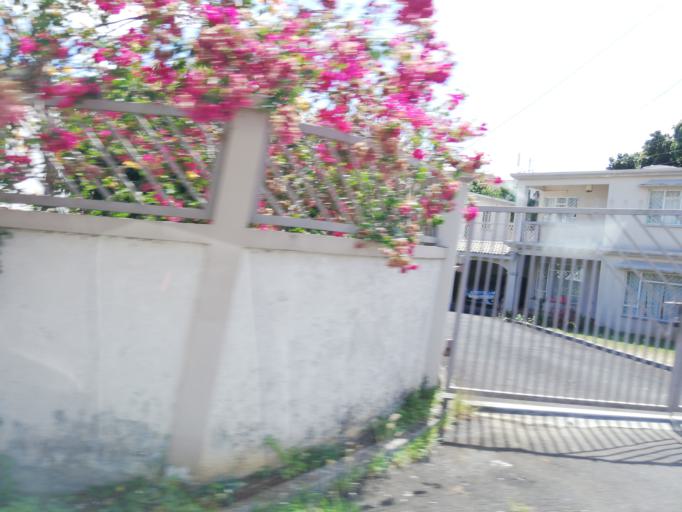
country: MU
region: Plaines Wilhems
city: Ebene
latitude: -20.2339
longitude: 57.4644
